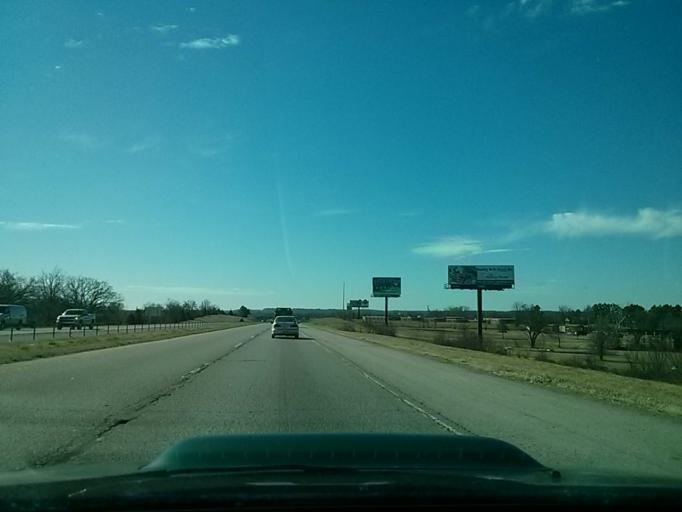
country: US
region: Oklahoma
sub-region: Tulsa County
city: Jenks
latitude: 36.0383
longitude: -96.0084
